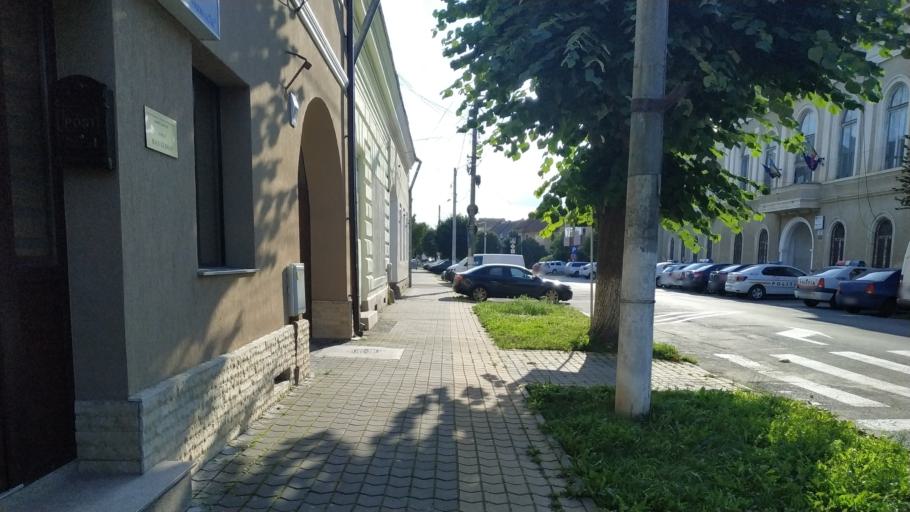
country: RO
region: Brasov
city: Fogarasch
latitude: 45.8443
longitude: 24.9657
